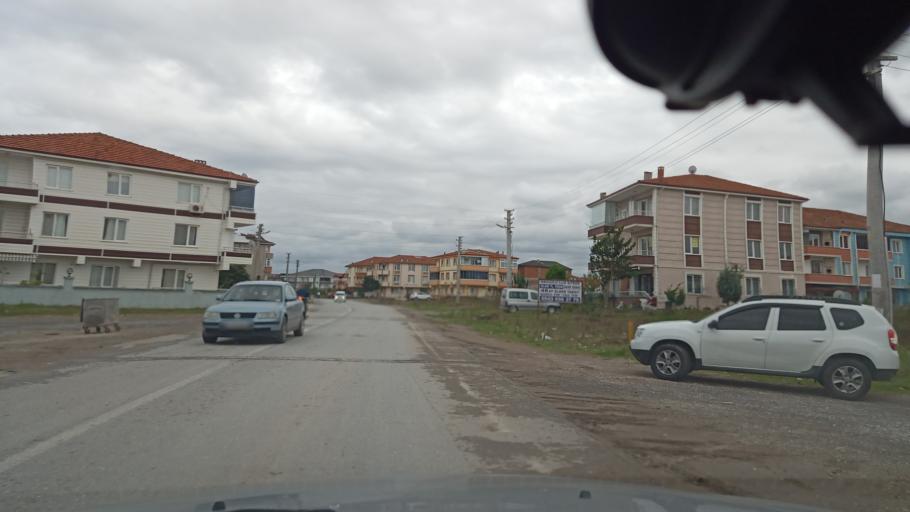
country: TR
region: Sakarya
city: Karasu
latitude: 41.1102
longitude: 30.6823
